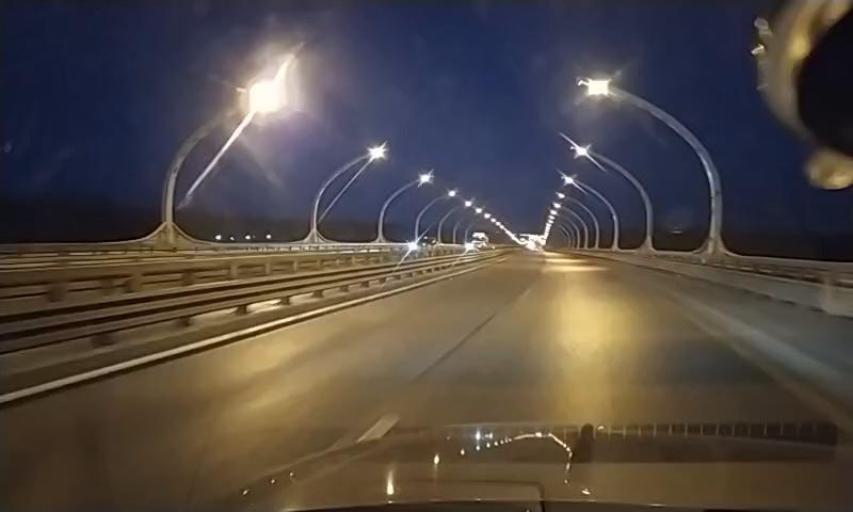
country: RU
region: St.-Petersburg
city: Beloostrov
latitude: 60.1370
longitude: 30.0546
